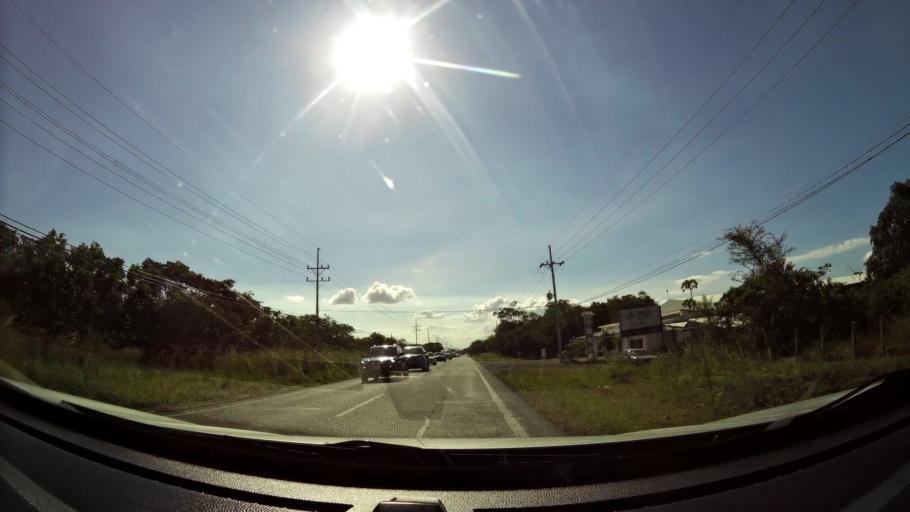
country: CR
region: Guanacaste
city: Liberia
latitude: 10.6027
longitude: -85.5149
